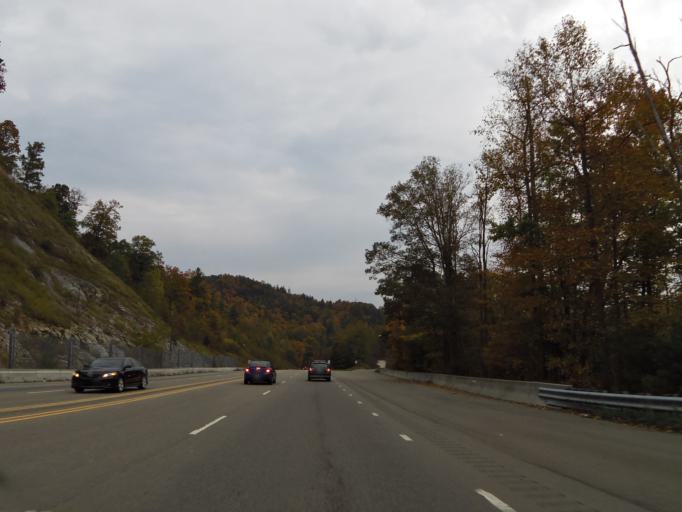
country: US
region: North Carolina
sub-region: Watauga County
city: Blowing Rock
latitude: 36.0487
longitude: -81.5941
